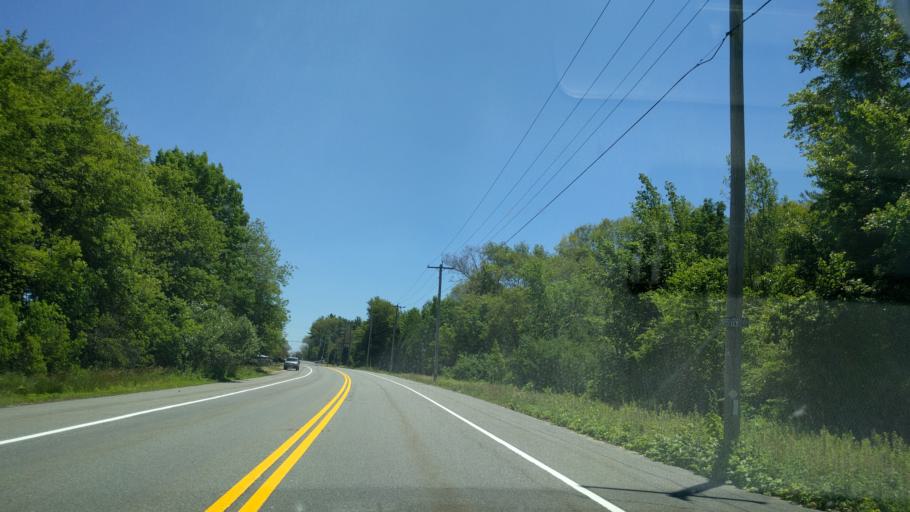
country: US
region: Massachusetts
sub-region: Worcester County
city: Millville
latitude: 42.0151
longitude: -71.5961
